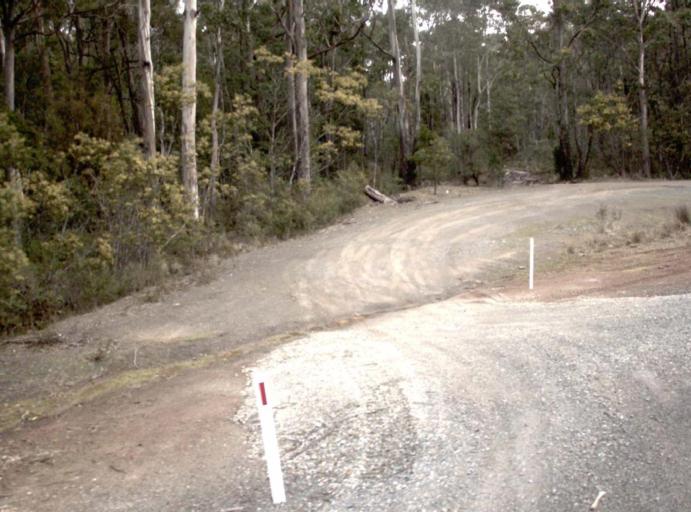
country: AU
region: Tasmania
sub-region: Launceston
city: Newstead
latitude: -41.3695
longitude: 147.2400
